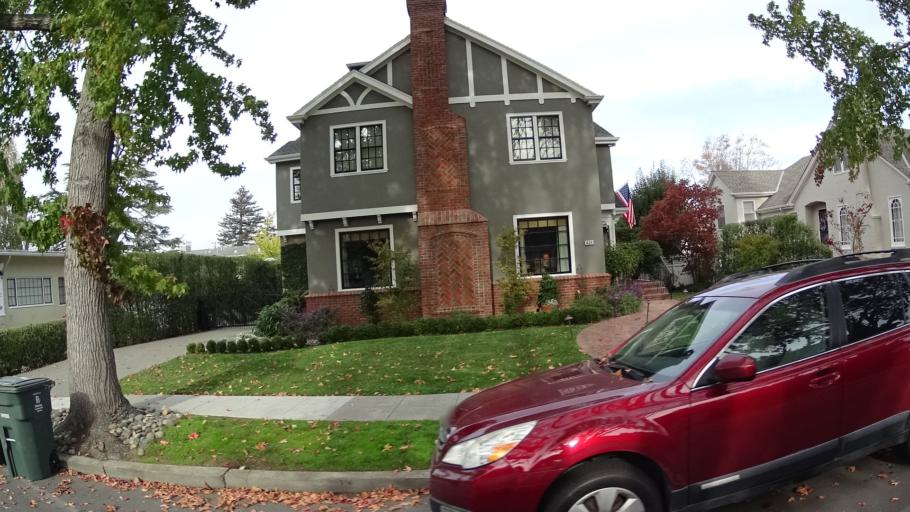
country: US
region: California
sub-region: San Mateo County
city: Hillsborough
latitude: 37.5826
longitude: -122.3780
